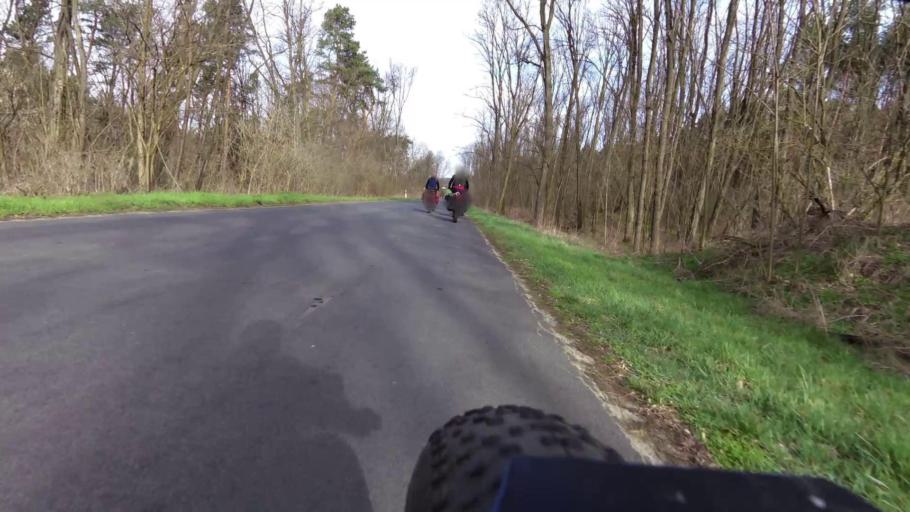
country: DE
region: Brandenburg
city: Brieskow-Finkenheerd
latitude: 52.2953
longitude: 14.6037
